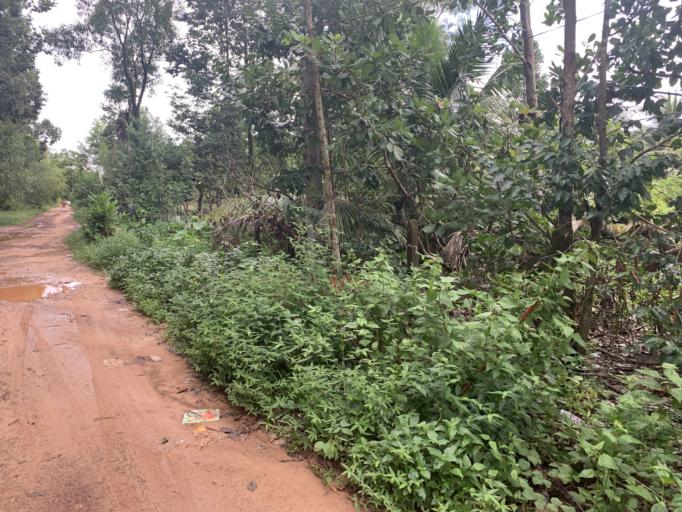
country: KH
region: Koh Kong
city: Koh Kong
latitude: 11.6231
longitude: 102.9816
